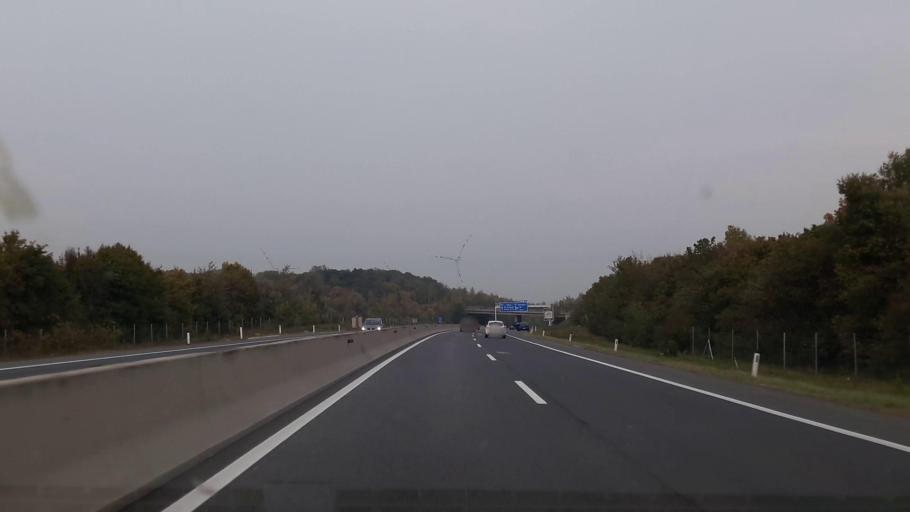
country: AT
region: Burgenland
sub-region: Politischer Bezirk Neusiedl am See
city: Parndorf
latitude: 47.9926
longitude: 16.8328
